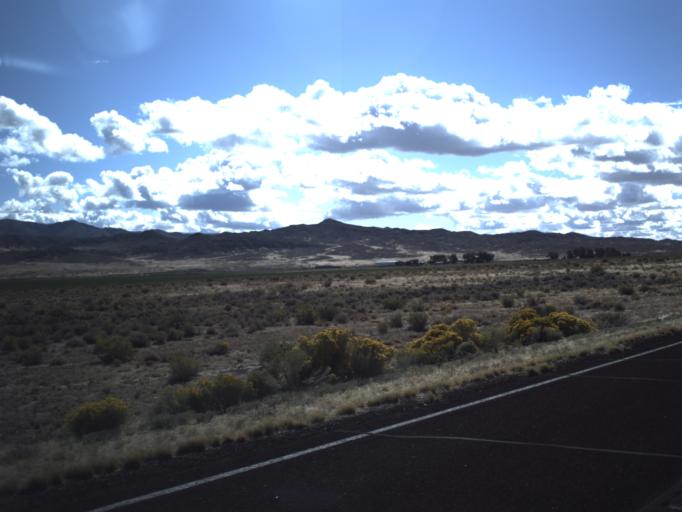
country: US
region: Nevada
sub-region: White Pine County
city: McGill
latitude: 38.9569
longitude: -114.0335
